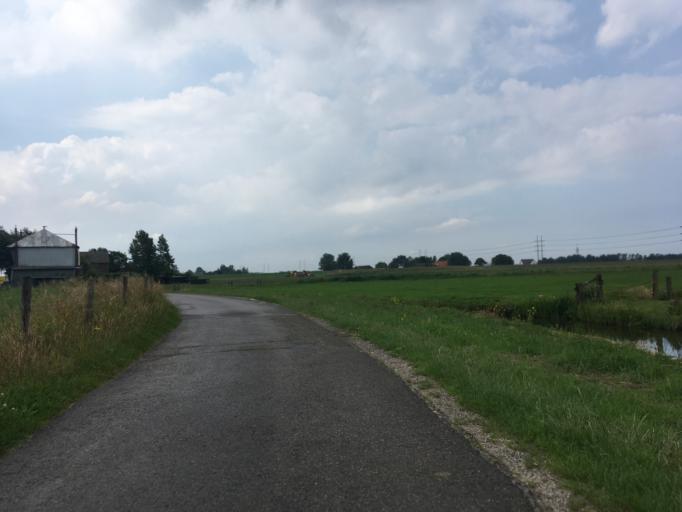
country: NL
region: North Holland
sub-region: Gemeente Haarlem
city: Haarlem
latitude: 52.4061
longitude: 4.7154
